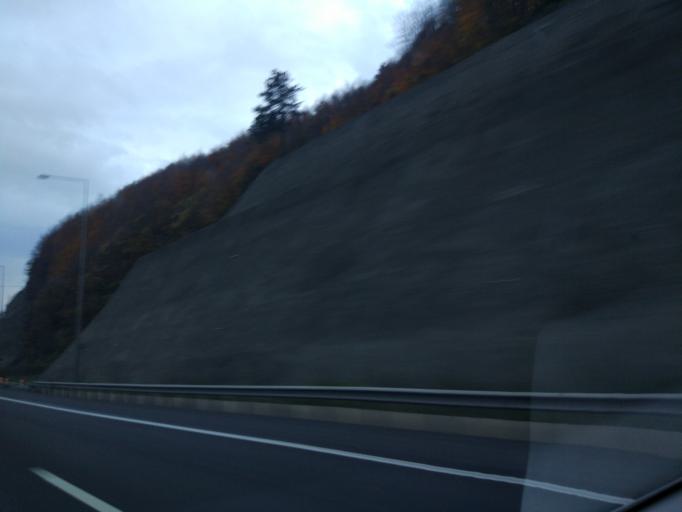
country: TR
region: Duzce
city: Kaynasli
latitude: 40.7614
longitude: 31.3980
